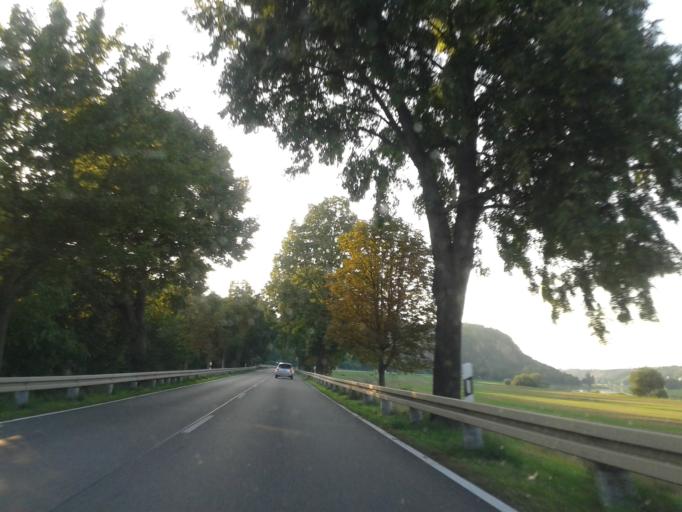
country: DE
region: Saxony
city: Meissen
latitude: 51.1717
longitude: 13.4677
